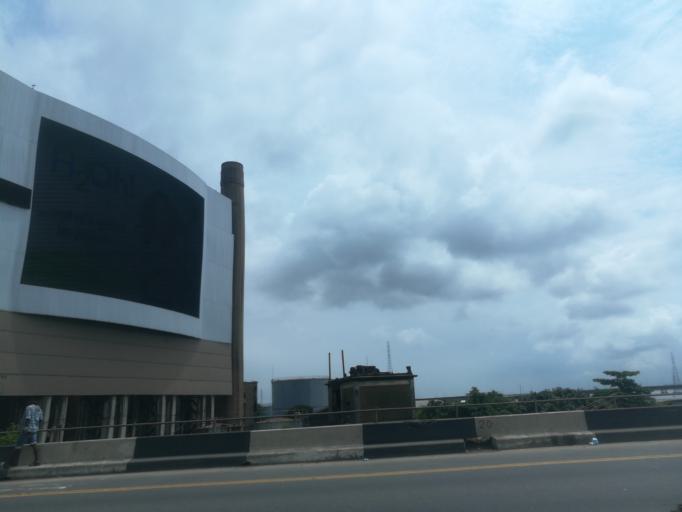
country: NG
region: Lagos
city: Lagos
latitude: 6.4667
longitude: 3.3790
